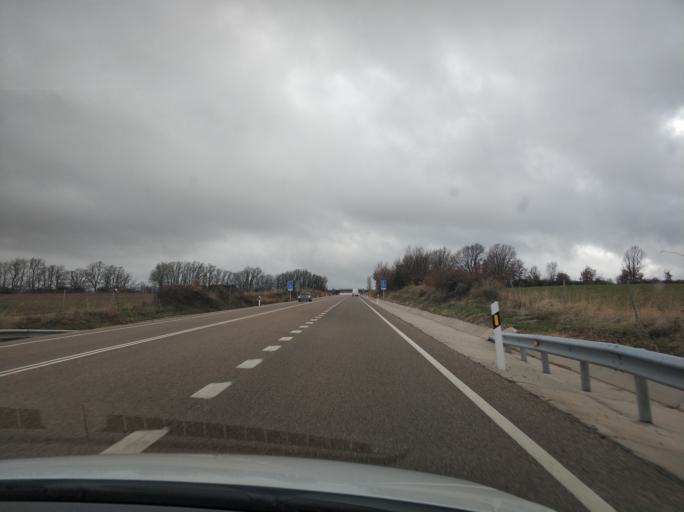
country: ES
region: Castille and Leon
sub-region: Provincia de Segovia
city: Riaza
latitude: 41.2905
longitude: -3.4800
